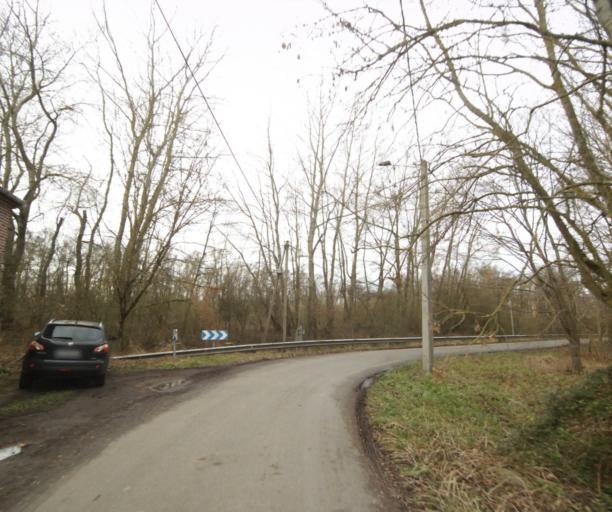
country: FR
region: Nord-Pas-de-Calais
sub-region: Departement du Nord
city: Bruille-Saint-Amand
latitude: 50.4832
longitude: 3.5006
